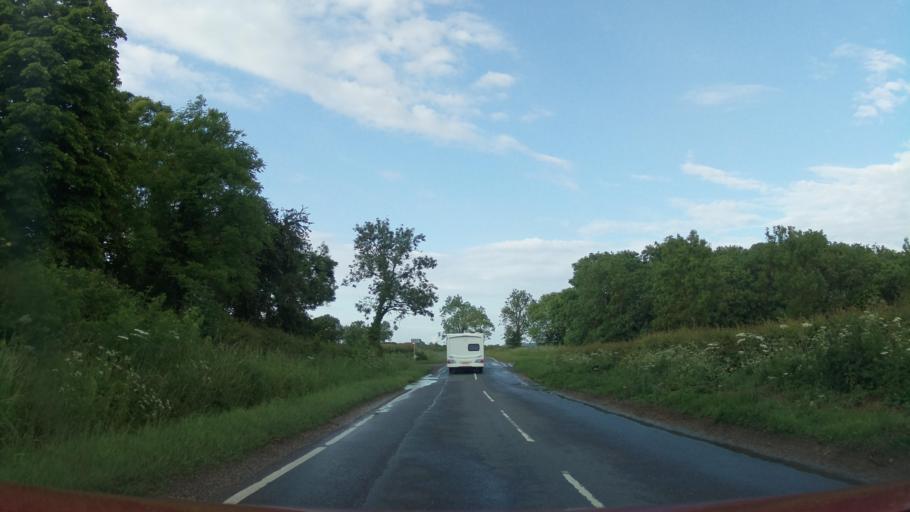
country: GB
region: England
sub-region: Lincolnshire
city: Great Gonerby
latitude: 53.0165
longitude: -0.6608
